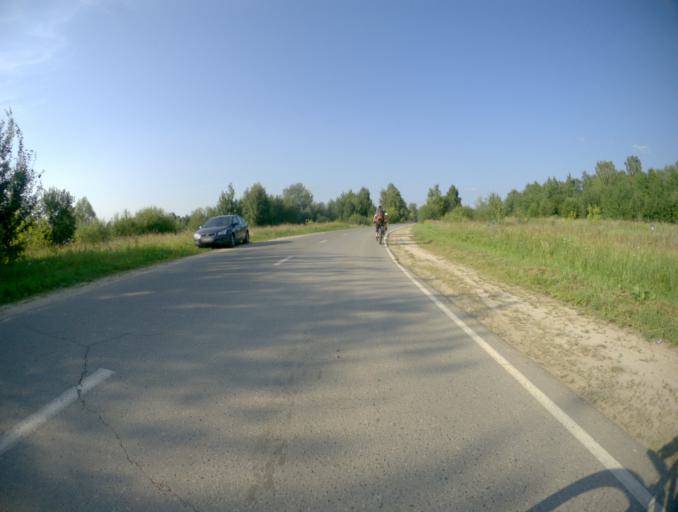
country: RU
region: Nizjnij Novgorod
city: Bor
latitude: 56.3442
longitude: 44.0469
